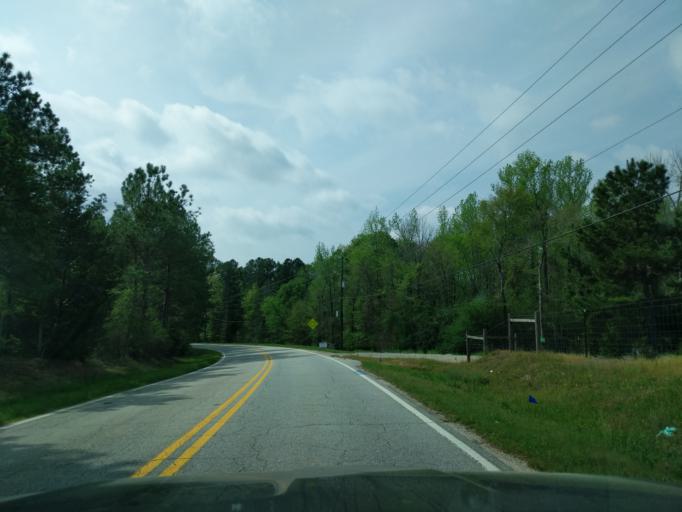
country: US
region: Georgia
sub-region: Columbia County
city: Appling
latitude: 33.5975
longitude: -82.3204
